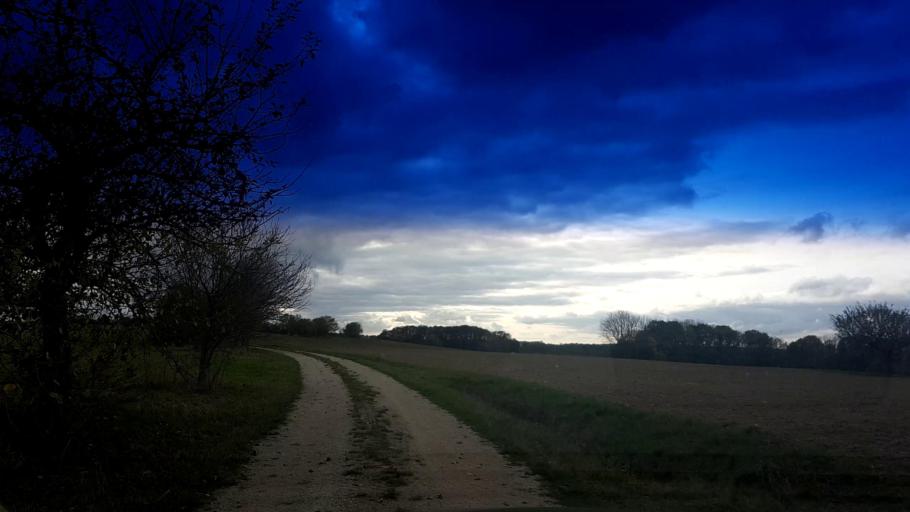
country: DE
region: Bavaria
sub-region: Upper Franconia
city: Schesslitz
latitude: 49.9873
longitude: 11.0253
